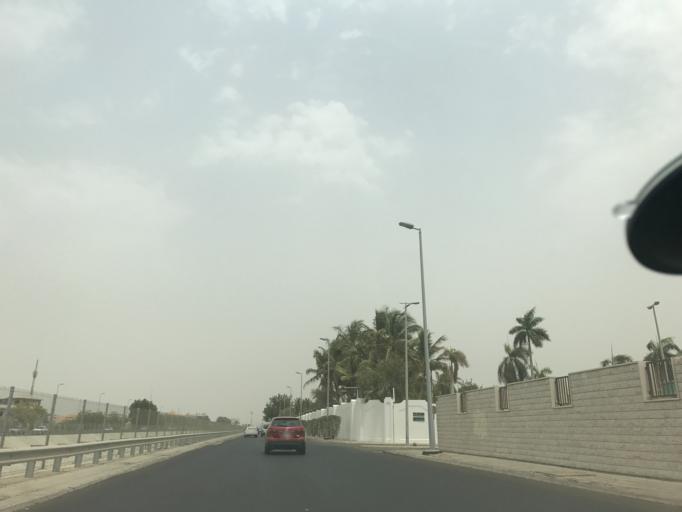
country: SA
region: Makkah
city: Jeddah
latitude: 21.5513
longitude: 39.1492
